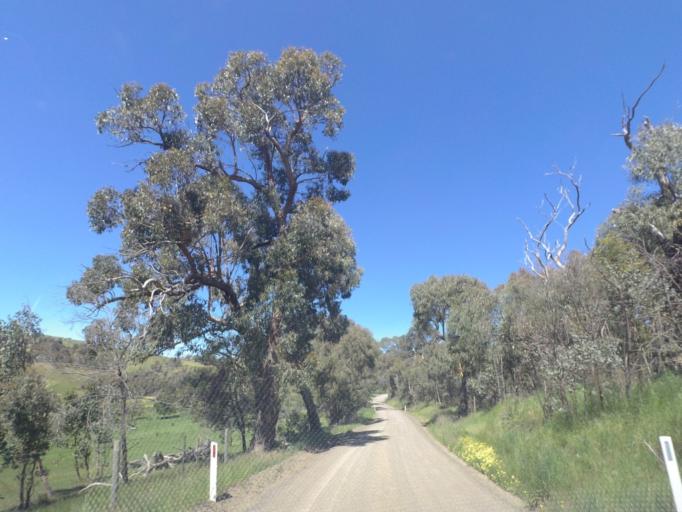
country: AU
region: Victoria
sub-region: Whittlesea
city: Whittlesea
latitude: -37.2775
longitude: 145.0158
